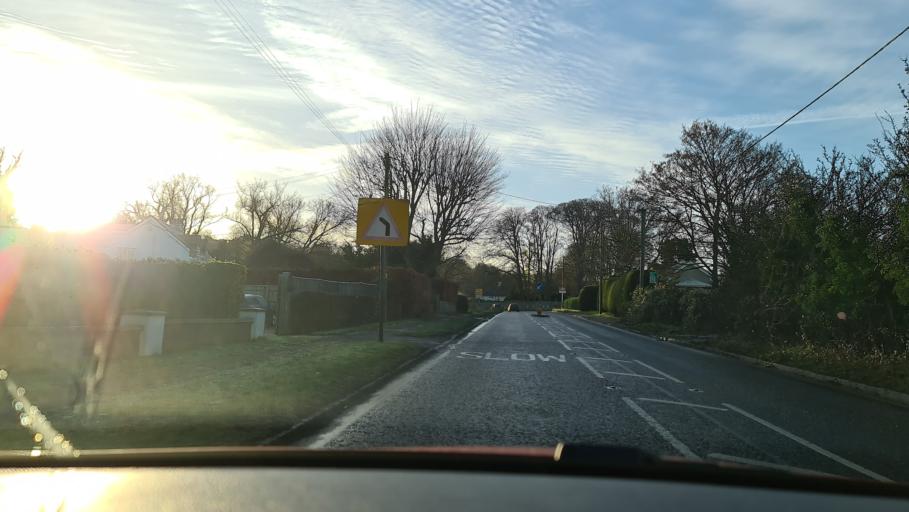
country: GB
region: England
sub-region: Buckinghamshire
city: Princes Risborough
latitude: 51.7532
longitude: -0.8082
